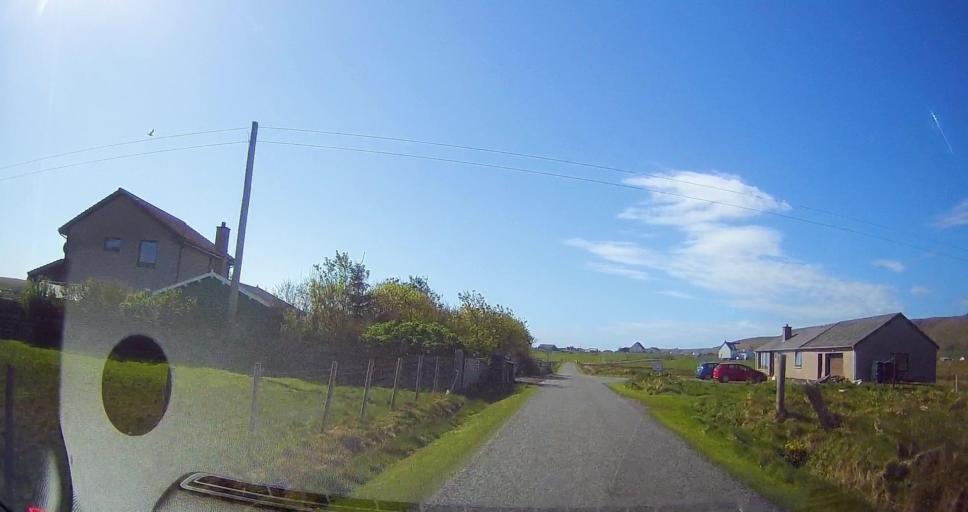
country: GB
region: Scotland
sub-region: Shetland Islands
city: Sandwick
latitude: 60.0441
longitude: -1.2172
